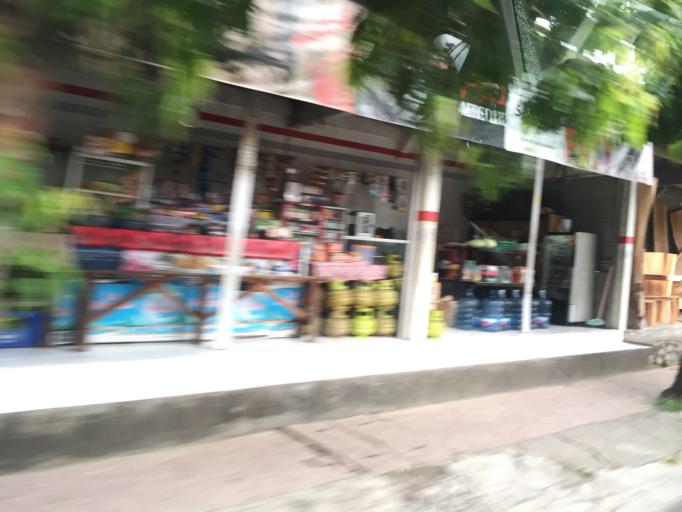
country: ID
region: Bali
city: Banjar Desa
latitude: -8.5779
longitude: 115.2771
